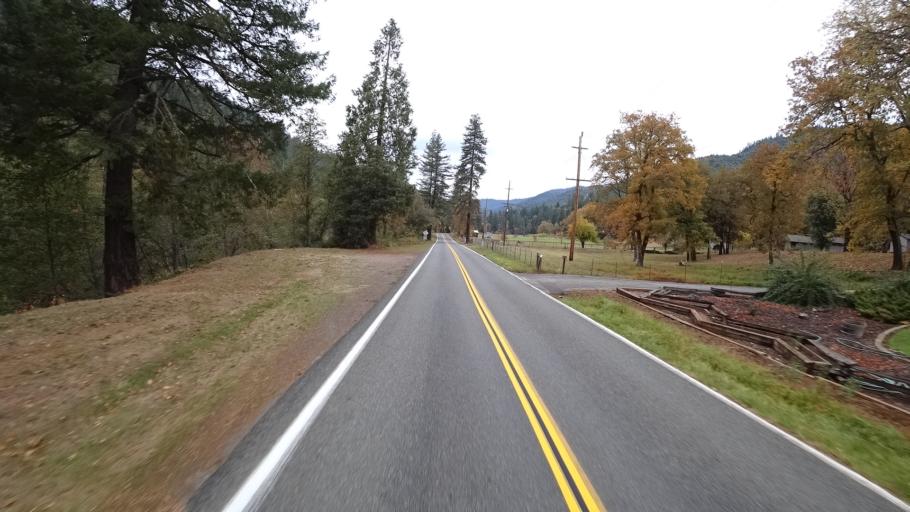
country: US
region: California
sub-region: Siskiyou County
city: Happy Camp
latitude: 41.8344
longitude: -123.3820
